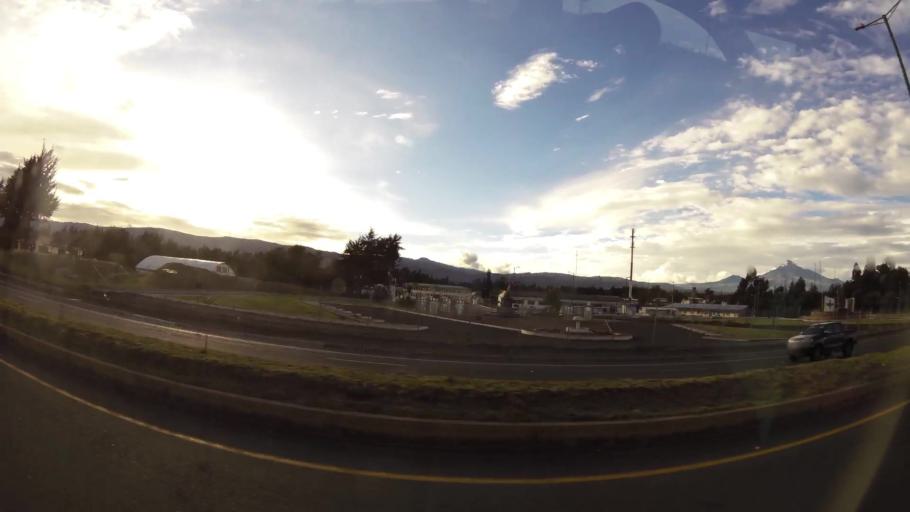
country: EC
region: Cotopaxi
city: Saquisili
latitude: -0.8531
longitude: -78.6198
